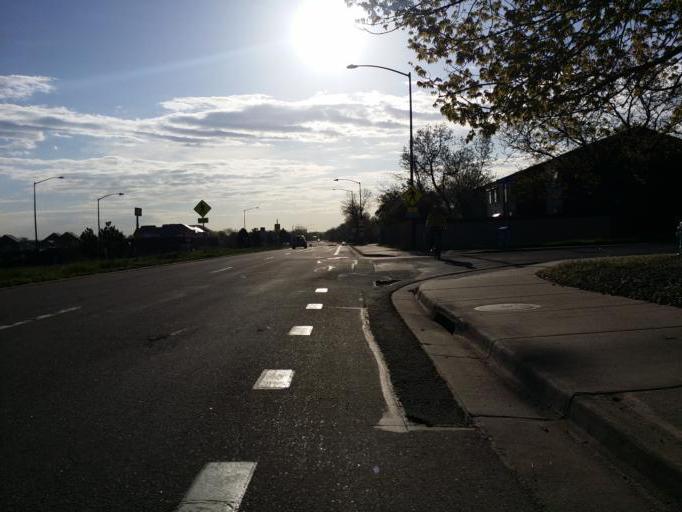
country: US
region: Colorado
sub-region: Boulder County
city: Boulder
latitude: 40.0073
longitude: -105.2491
